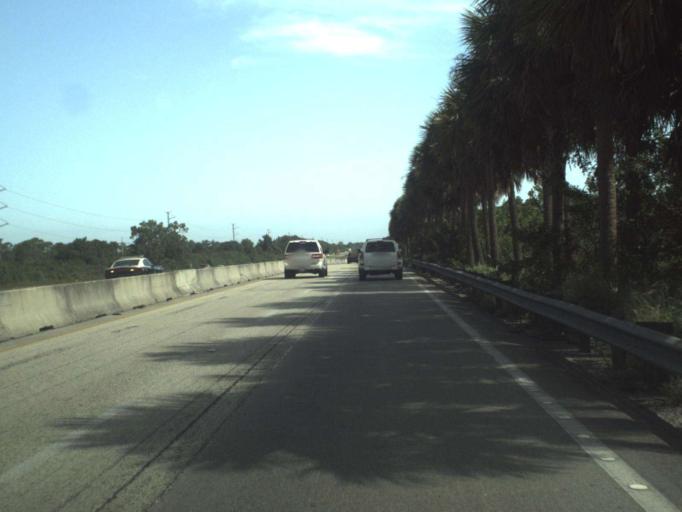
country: US
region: Florida
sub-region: Indian River County
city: West Vero Corridor
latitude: 27.6833
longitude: -80.5344
